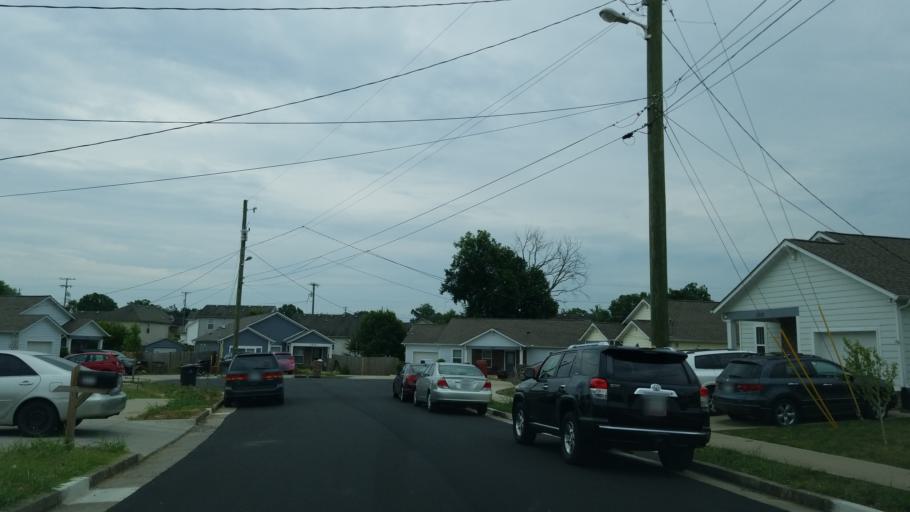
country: US
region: Tennessee
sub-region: Rutherford County
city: La Vergne
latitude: 36.0519
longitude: -86.5928
